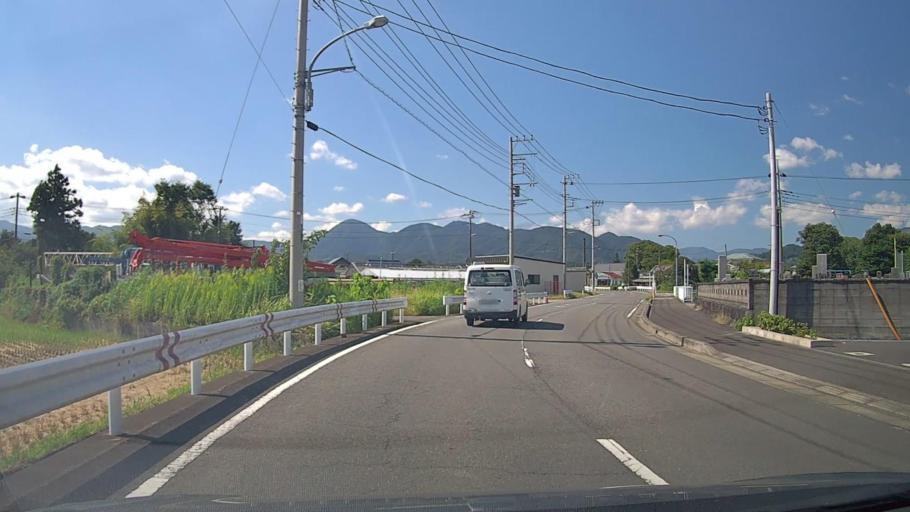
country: JP
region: Kanagawa
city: Odawara
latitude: 35.3426
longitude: 139.1147
